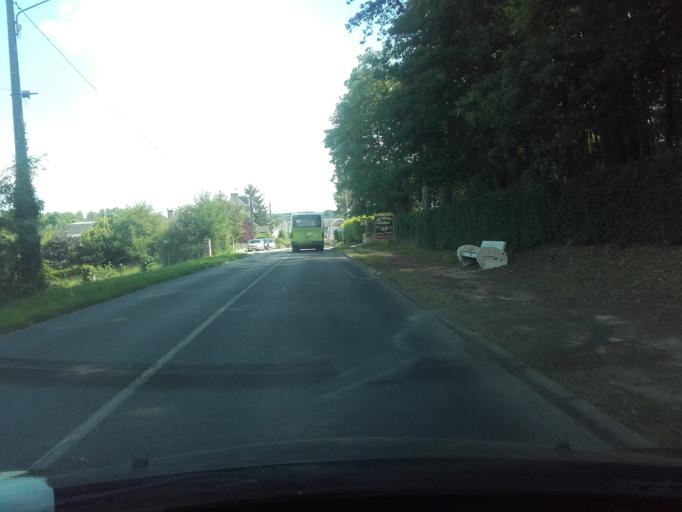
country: FR
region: Centre
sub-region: Departement d'Indre-et-Loire
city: Cinq-Mars-la-Pile
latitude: 47.3468
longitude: 0.4519
